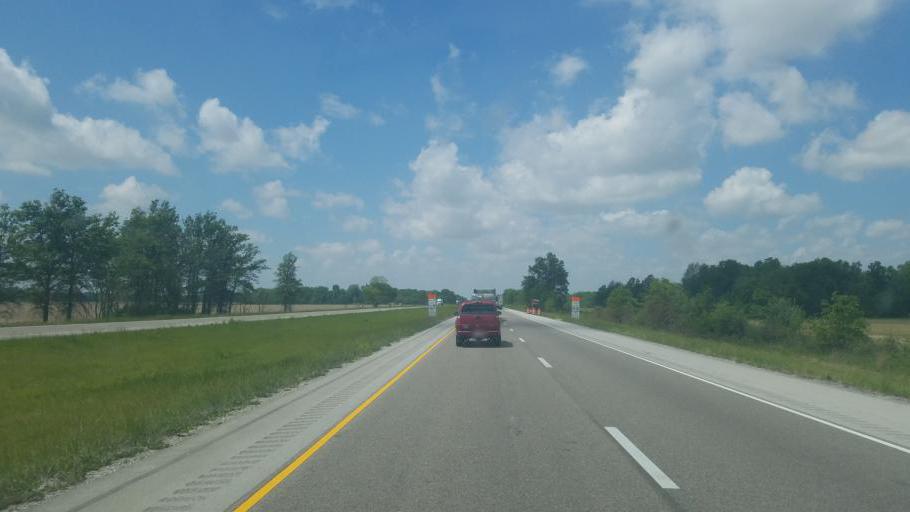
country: US
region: Illinois
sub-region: Cumberland County
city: Toledo
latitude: 39.2270
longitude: -88.2231
